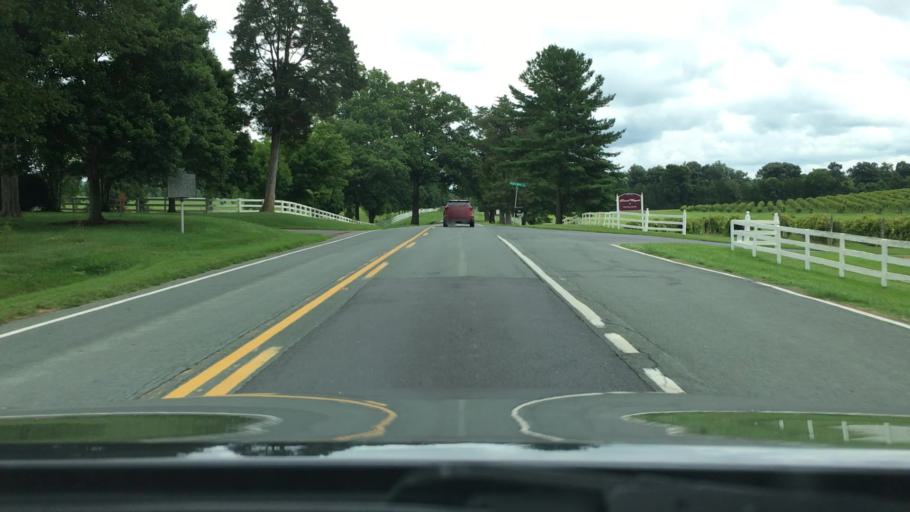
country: US
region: Virginia
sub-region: Orange County
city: Gordonsville
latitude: 38.0771
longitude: -78.2924
